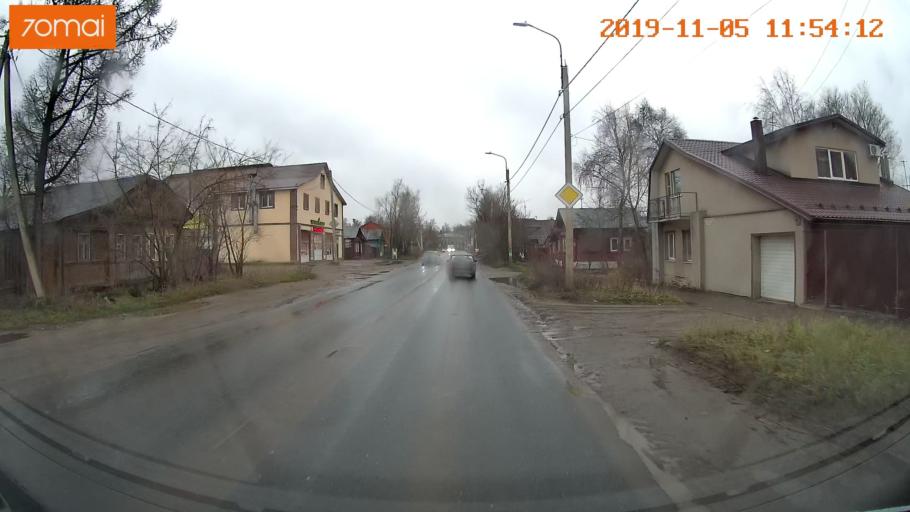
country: RU
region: Ivanovo
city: Bogorodskoye
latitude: 56.9921
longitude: 41.0311
